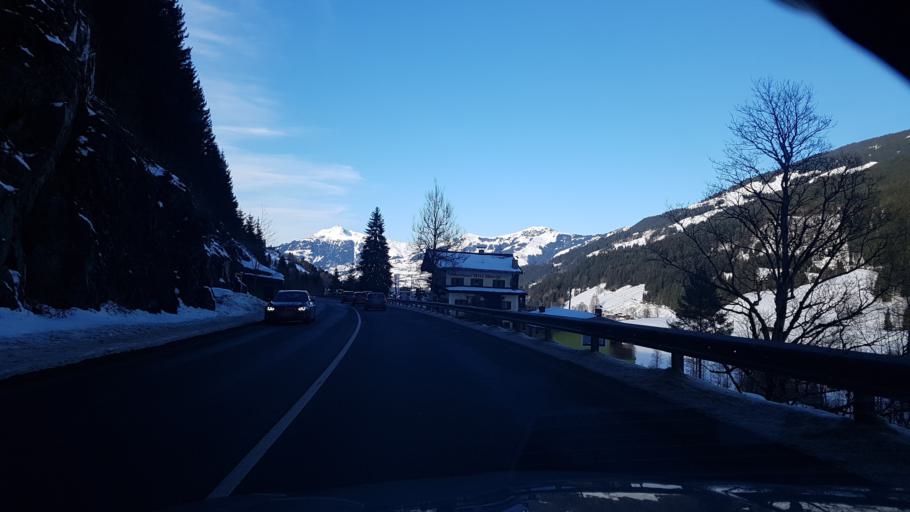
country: AT
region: Tyrol
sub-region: Politischer Bezirk Kitzbuhel
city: Jochberg
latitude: 47.3535
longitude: 12.4142
